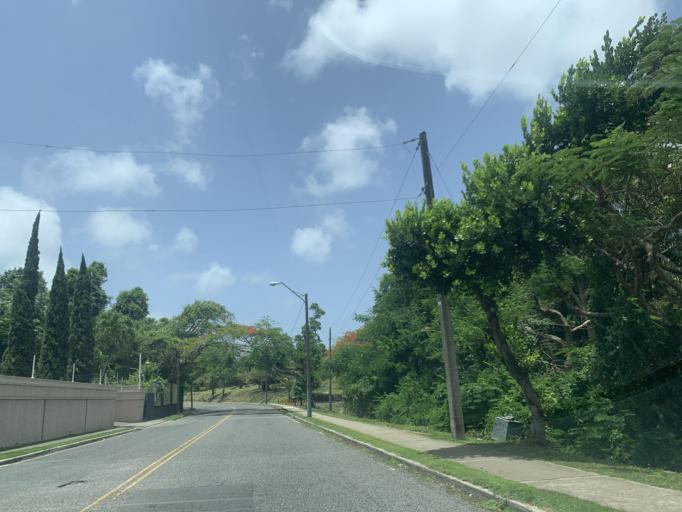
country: DO
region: Nacional
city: La Agustina
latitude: 18.4942
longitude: -69.9492
